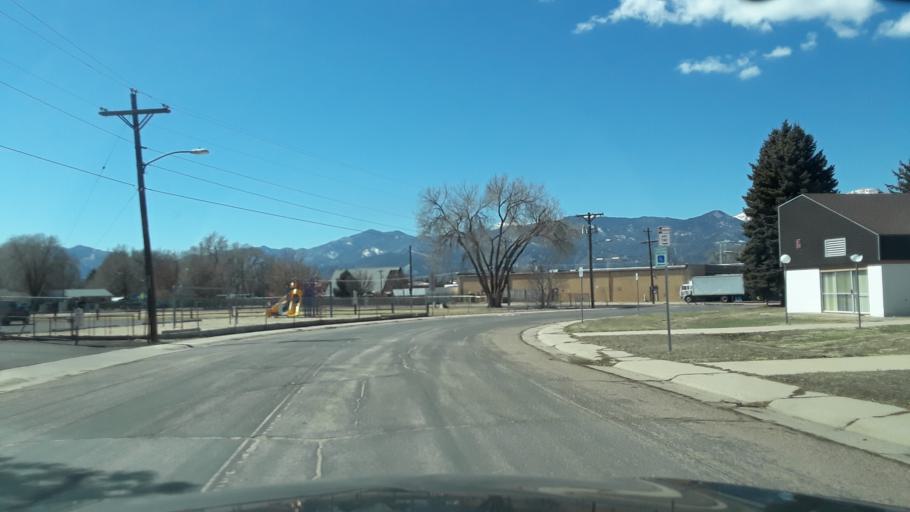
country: US
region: Colorado
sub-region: El Paso County
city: Colorado Springs
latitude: 38.8763
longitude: -104.8008
